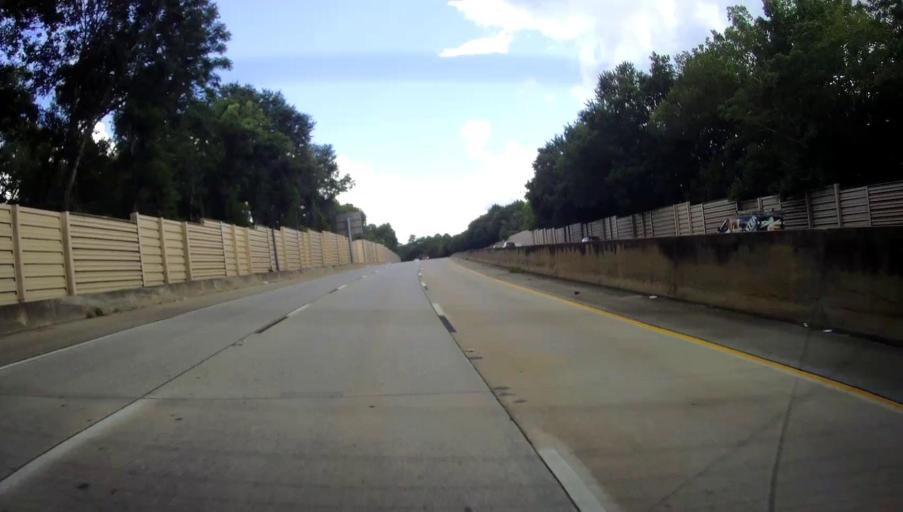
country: US
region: Georgia
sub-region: Muscogee County
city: Columbus
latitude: 32.4929
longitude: -84.9430
